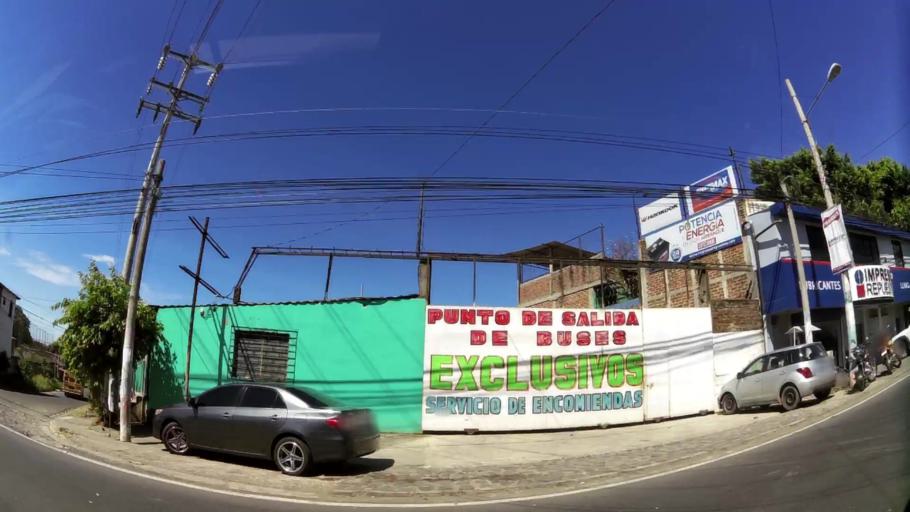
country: SV
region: Ahuachapan
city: Ahuachapan
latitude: 13.9267
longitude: -89.8408
